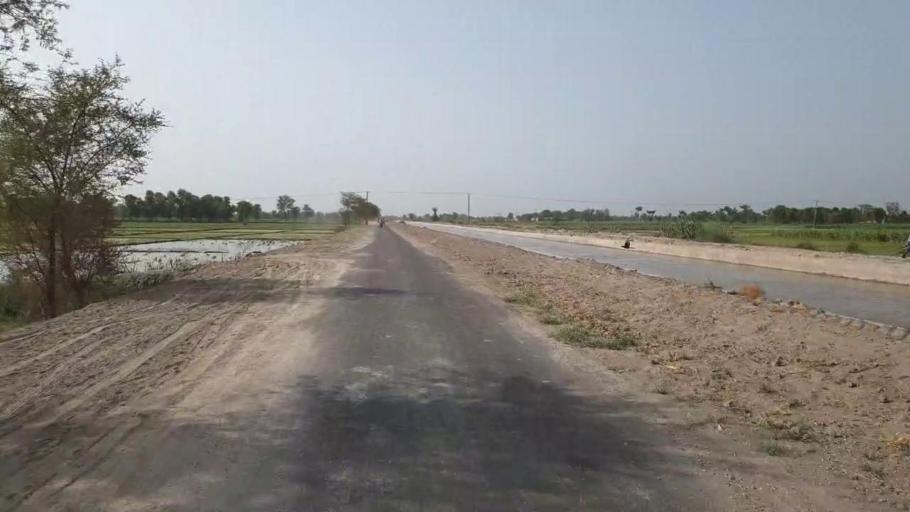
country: PK
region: Sindh
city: Daur
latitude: 26.3456
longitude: 68.1621
